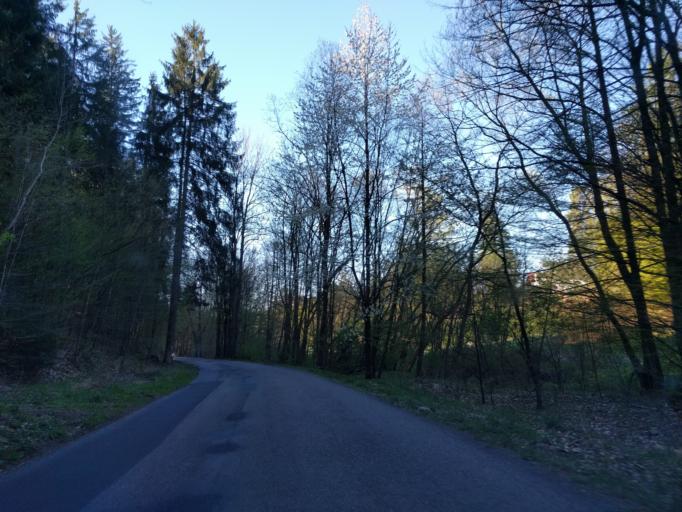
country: CZ
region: Central Bohemia
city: Ondrejov
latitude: 49.8976
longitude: 14.7387
